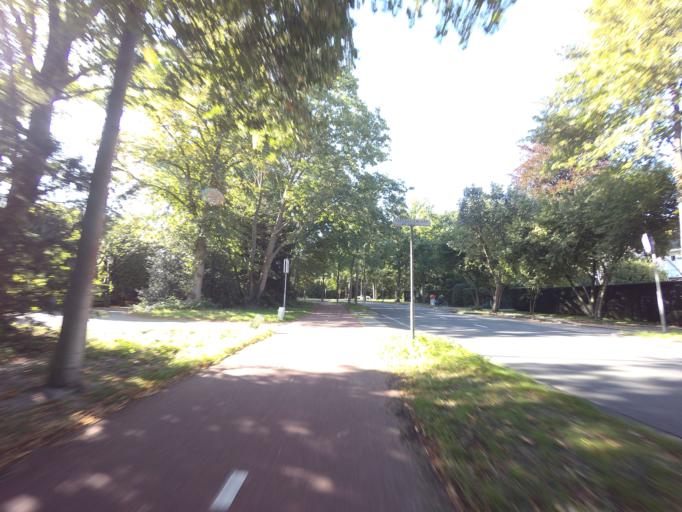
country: NL
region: South Holland
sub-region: Gemeente Wassenaar
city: Wassenaar
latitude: 52.1314
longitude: 4.3834
